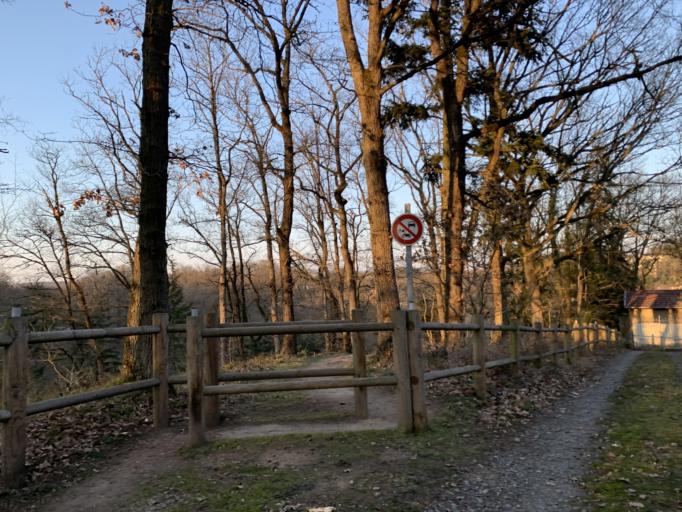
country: FR
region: Rhone-Alpes
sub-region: Departement du Rhone
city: Charbonnieres-les-Bains
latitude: 45.7840
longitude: 4.7326
